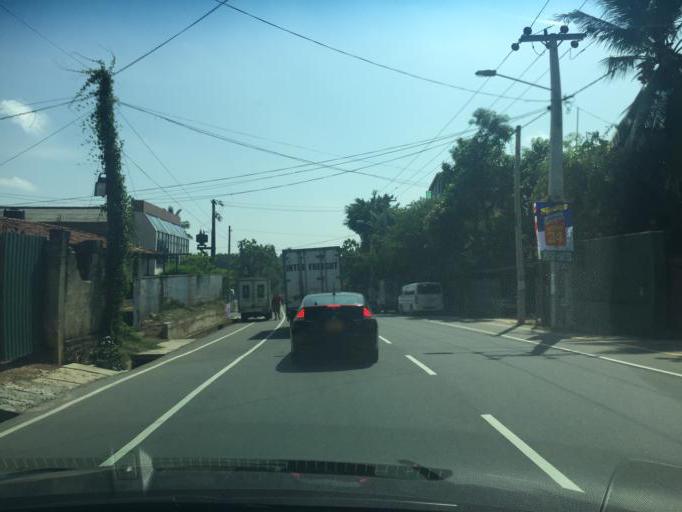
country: LK
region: Western
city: Sri Jayewardenepura Kotte
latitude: 6.8609
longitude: 79.8950
